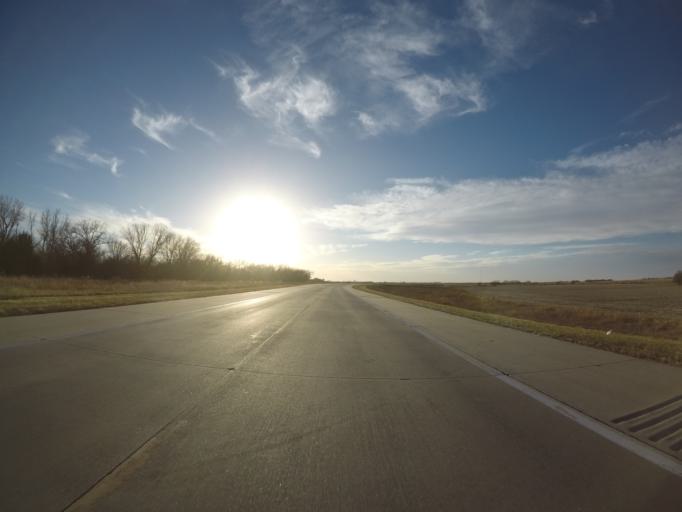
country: US
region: Kansas
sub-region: Chase County
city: Cottonwood Falls
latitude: 38.4055
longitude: -96.3875
